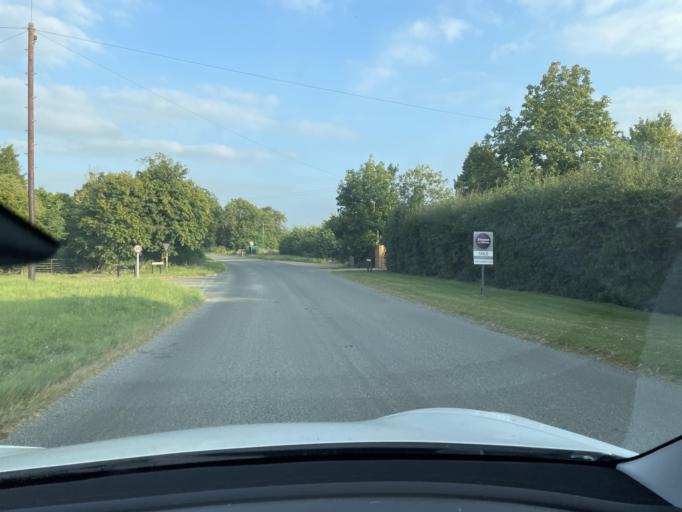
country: GB
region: England
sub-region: Bedford
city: Swineshead
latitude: 52.3690
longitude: -0.4483
